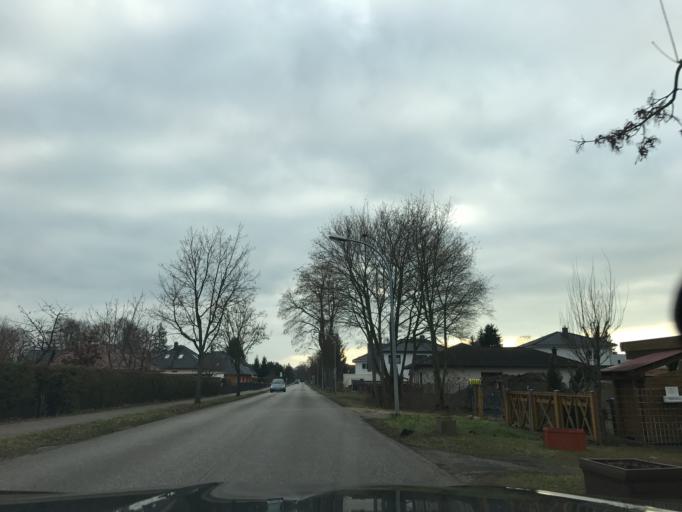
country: DE
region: Brandenburg
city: Brandenburg an der Havel
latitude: 52.3796
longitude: 12.5452
